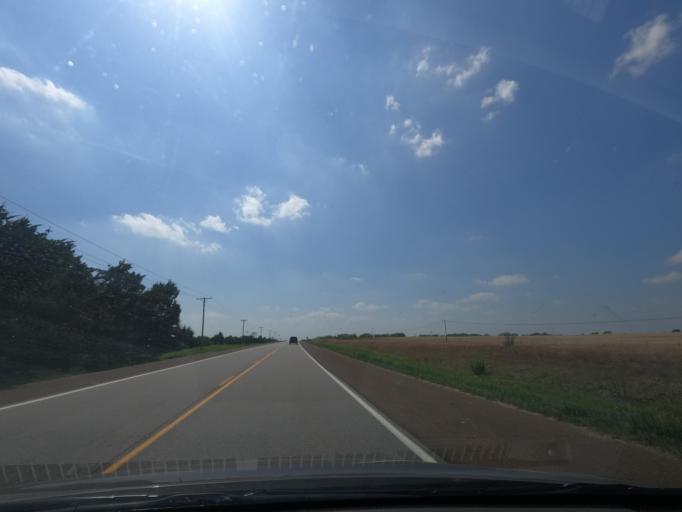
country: US
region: Kansas
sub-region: Butler County
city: El Dorado
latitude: 37.6794
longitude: -96.8025
